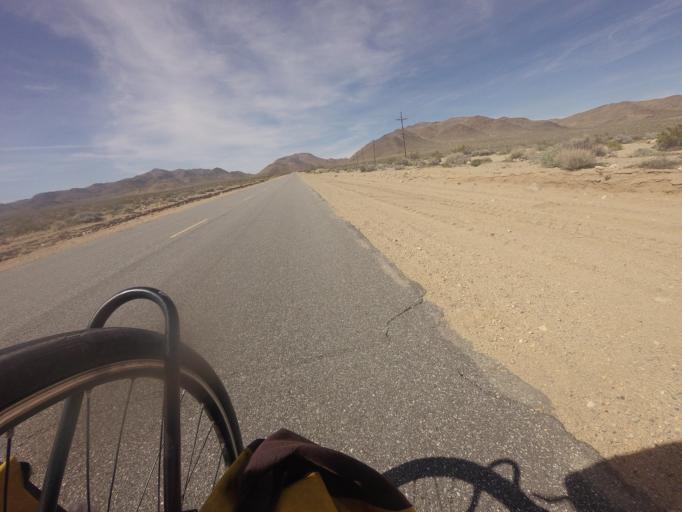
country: US
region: California
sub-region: San Bernardino County
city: Searles Valley
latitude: 35.5716
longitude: -117.4453
